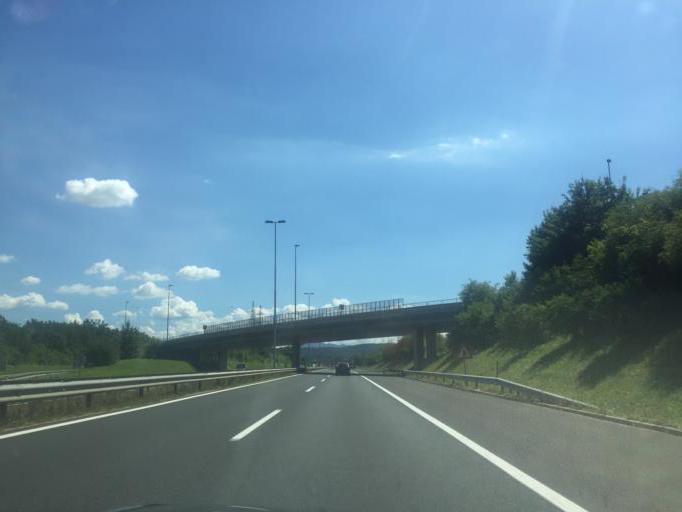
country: SI
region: Dol pri Ljubljani
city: Dol pri Ljubljani
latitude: 46.0675
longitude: 14.5765
